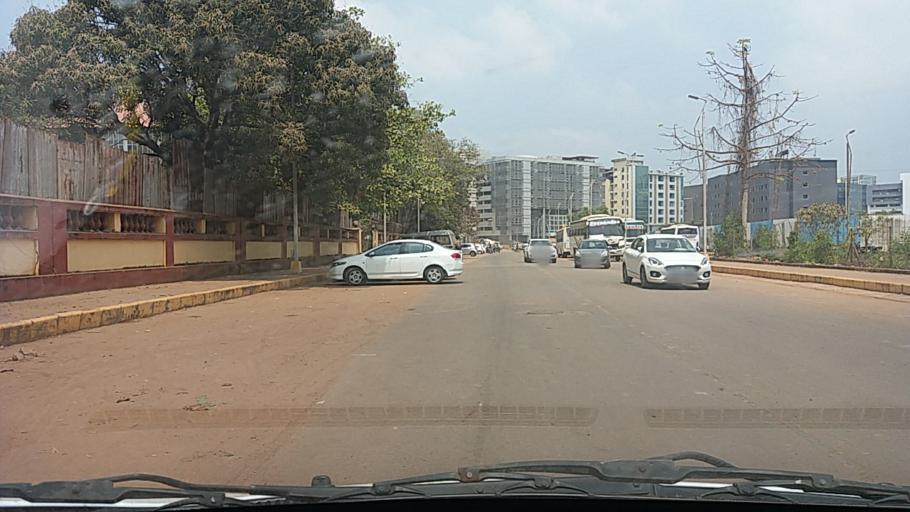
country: IN
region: Goa
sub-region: North Goa
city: Panaji
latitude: 15.4927
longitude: 73.8336
